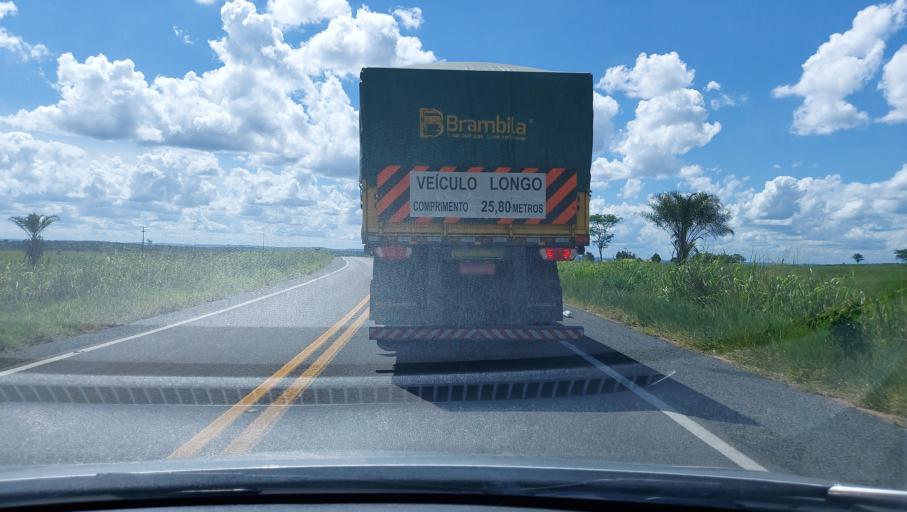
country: BR
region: Bahia
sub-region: Ruy Barbosa
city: Terra Nova
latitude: -12.4452
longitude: -40.7121
